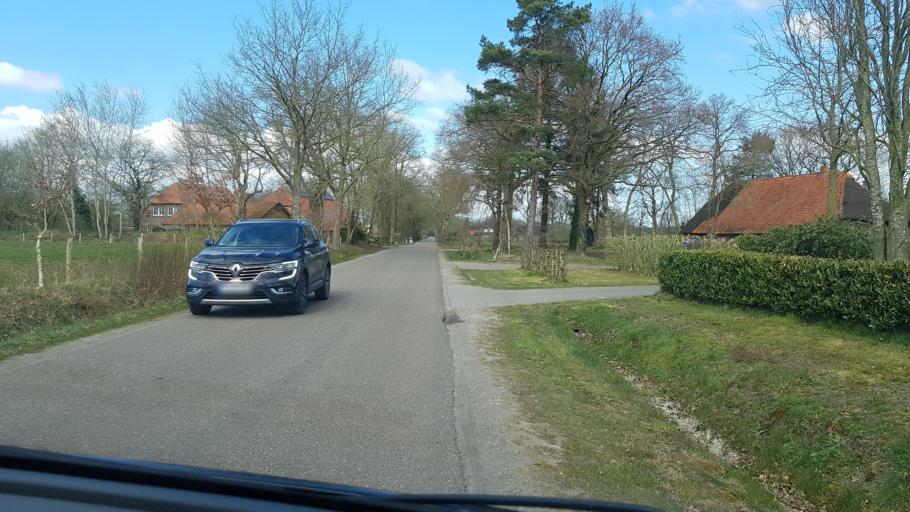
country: DE
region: Lower Saxony
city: Edewecht
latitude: 53.1628
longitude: 7.9372
